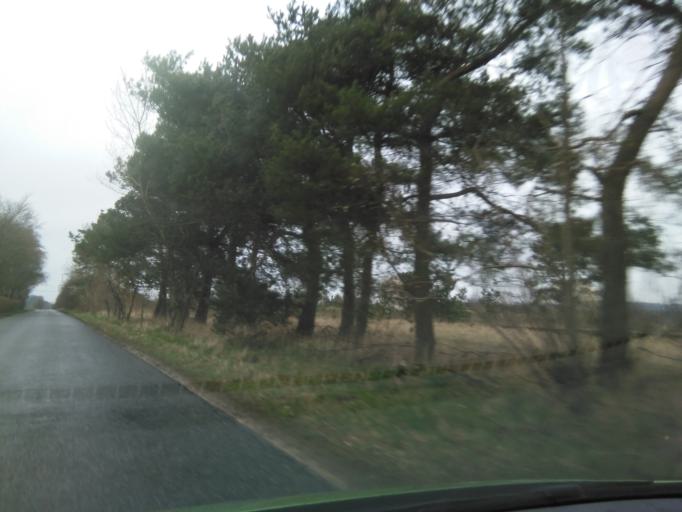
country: DK
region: Central Jutland
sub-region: Arhus Kommune
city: Kolt
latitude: 56.1397
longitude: 10.0511
